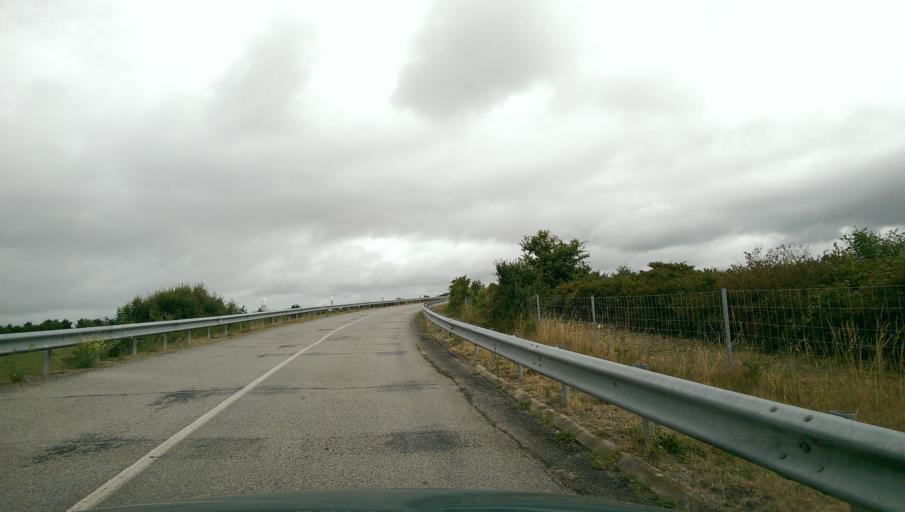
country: FR
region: Pays de la Loire
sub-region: Departement de la Loire-Atlantique
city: La Planche
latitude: 47.0277
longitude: -1.4057
